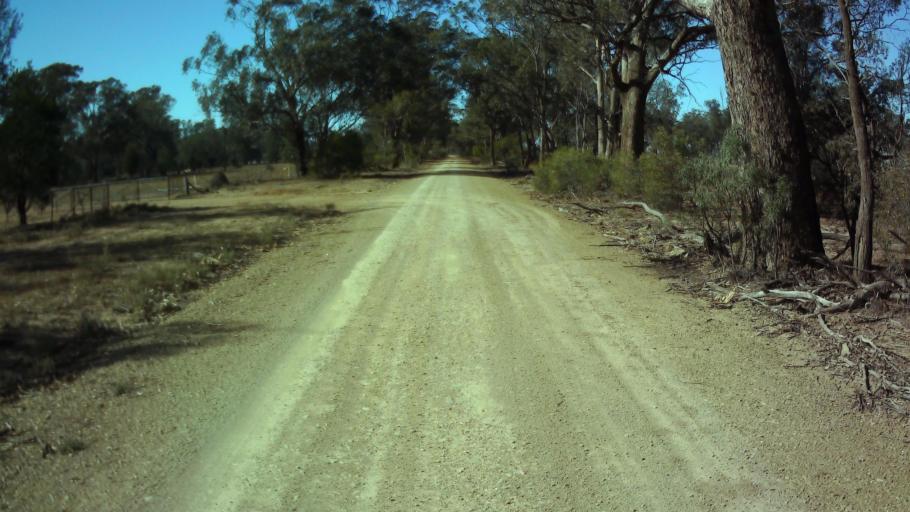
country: AU
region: New South Wales
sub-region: Weddin
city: Grenfell
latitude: -33.9371
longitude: 147.8717
